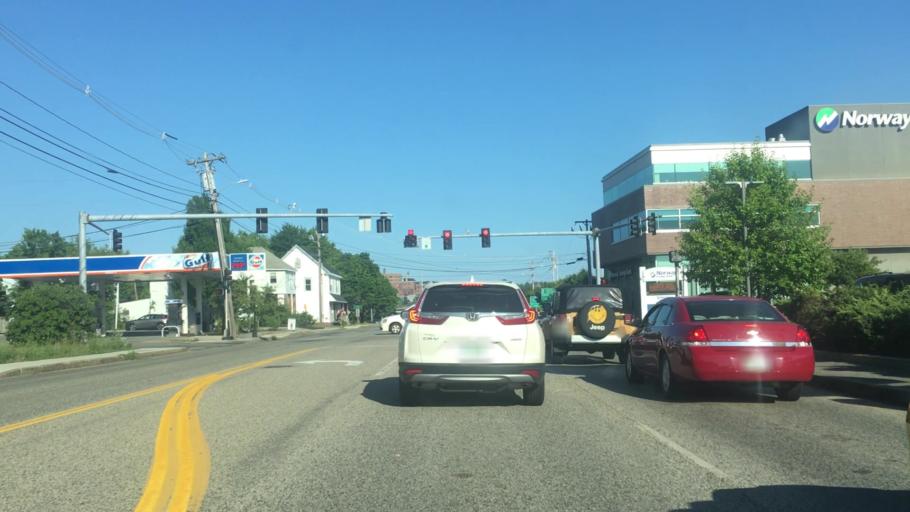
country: US
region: Maine
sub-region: Cumberland County
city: South Portland Gardens
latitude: 43.6572
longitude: -70.2896
